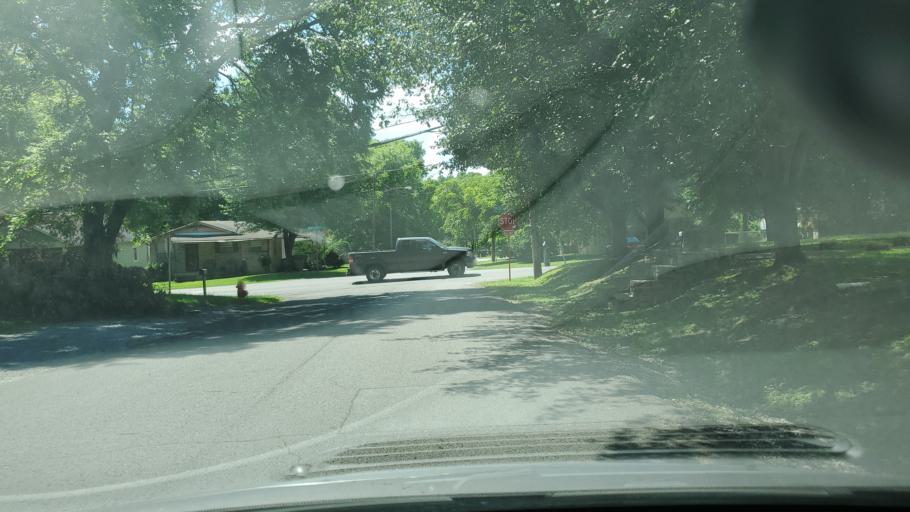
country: US
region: Tennessee
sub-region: Davidson County
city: Nashville
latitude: 36.1971
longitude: -86.7549
